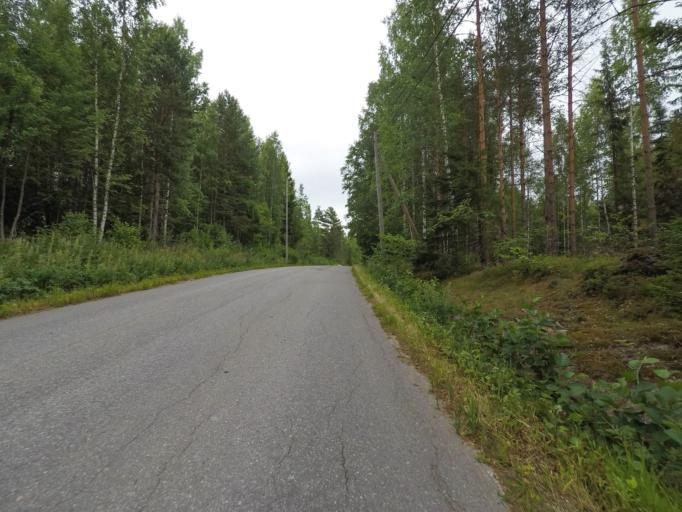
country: FI
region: Uusimaa
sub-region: Helsinki
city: Karjalohja
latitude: 60.2611
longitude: 23.7011
